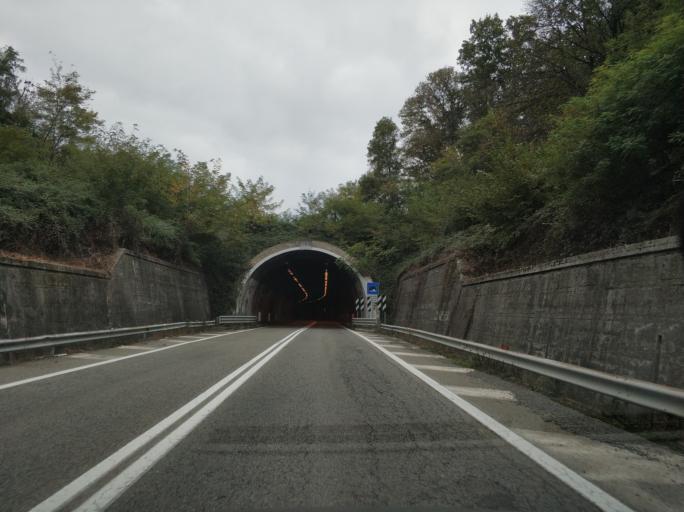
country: IT
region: Piedmont
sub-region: Provincia di Torino
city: Torre Canavese
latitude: 45.4027
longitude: 7.7561
